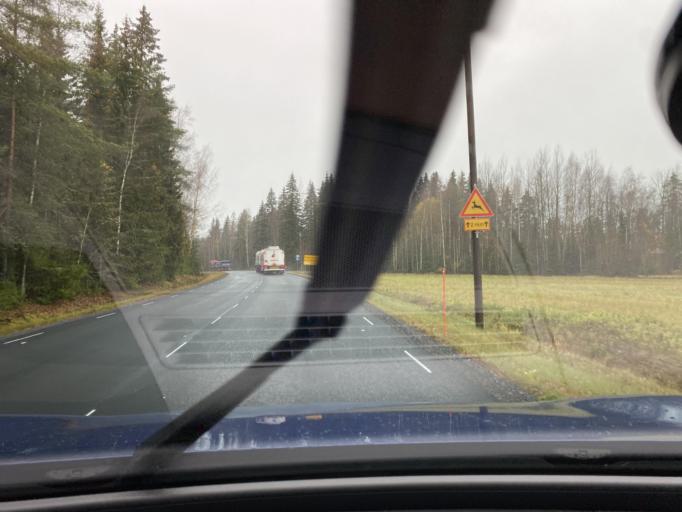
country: FI
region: Haeme
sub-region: Forssa
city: Ypaejae
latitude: 60.7730
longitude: 23.3444
